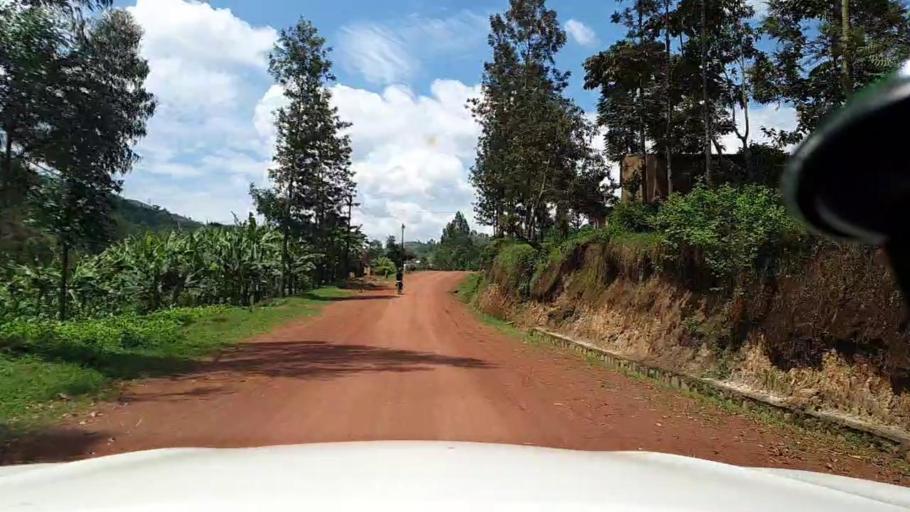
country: RW
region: Northern Province
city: Byumba
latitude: -1.7041
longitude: 29.8388
